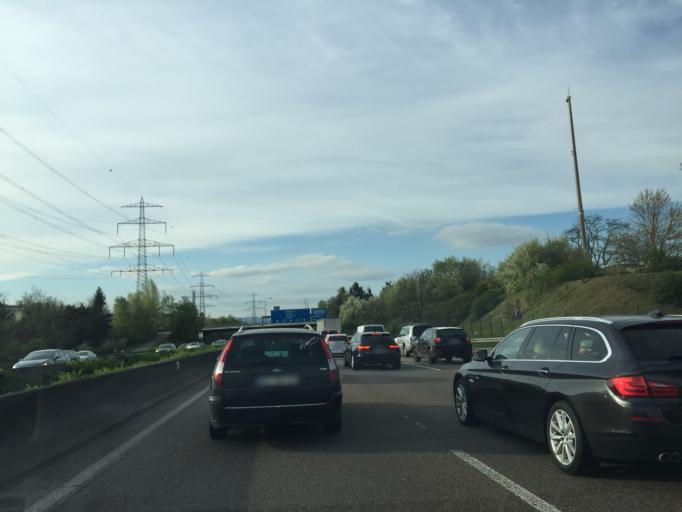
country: DE
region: Hesse
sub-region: Regierungsbezirk Darmstadt
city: Eschborn
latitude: 50.1209
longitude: 8.5950
